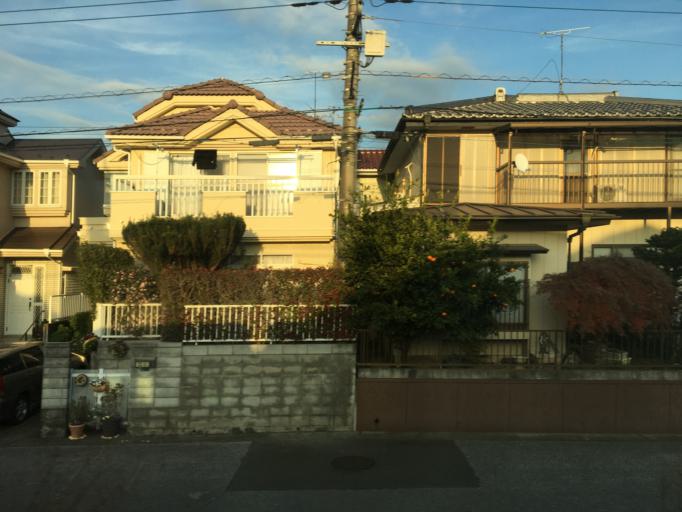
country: JP
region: Saitama
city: Fukiage-fujimi
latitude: 36.0827
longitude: 139.4799
